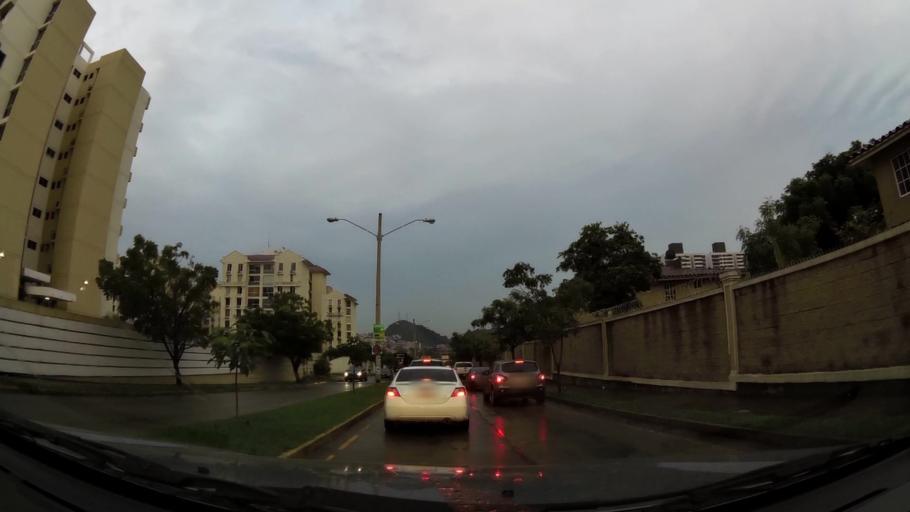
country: PA
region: Panama
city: Panama
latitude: 9.0360
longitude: -79.5309
